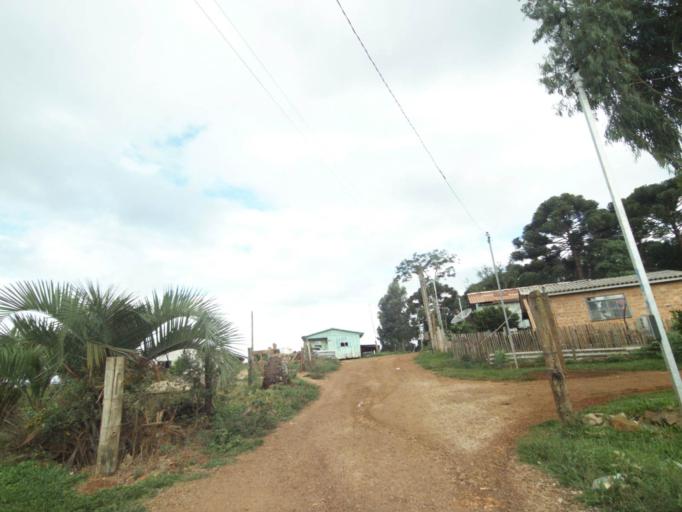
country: BR
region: Rio Grande do Sul
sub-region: Lagoa Vermelha
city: Lagoa Vermelha
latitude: -28.2020
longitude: -51.5082
